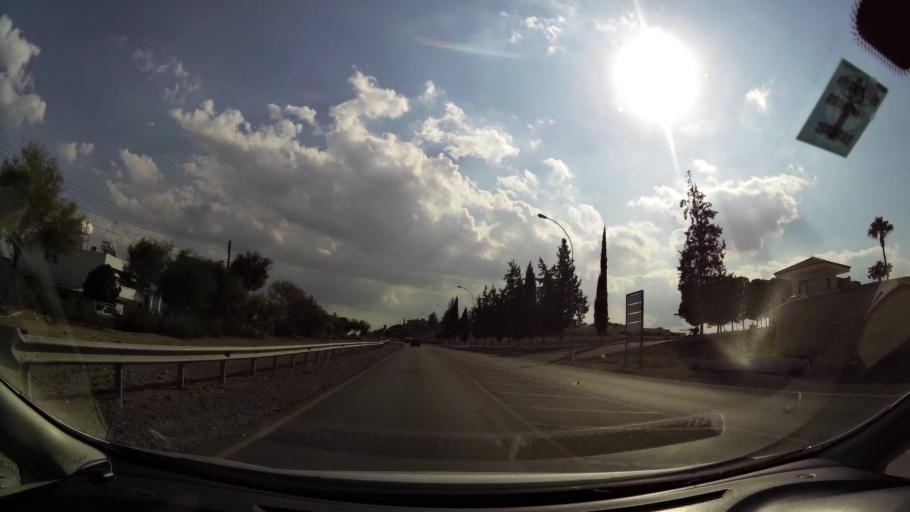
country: CY
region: Lefkosia
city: Nicosia
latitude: 35.1545
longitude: 33.3086
